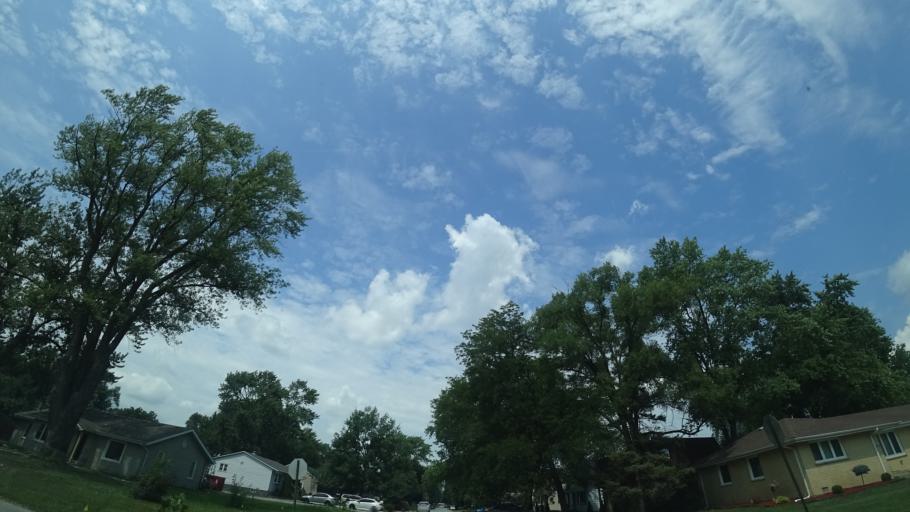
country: US
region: Illinois
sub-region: Cook County
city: Worth
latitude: 41.6846
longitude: -87.7859
